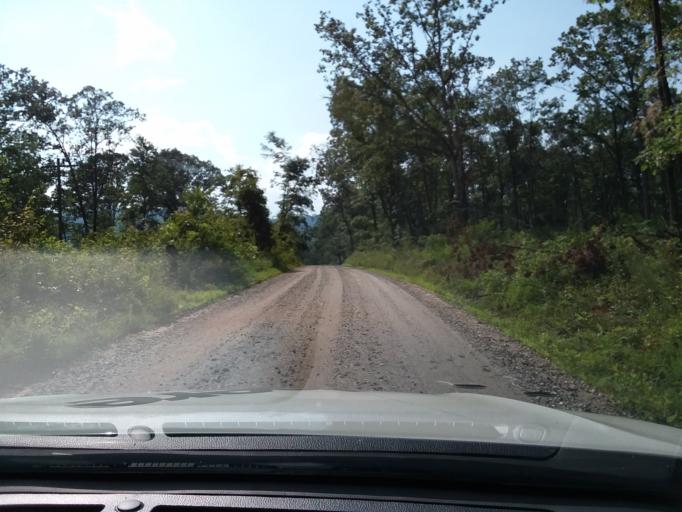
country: US
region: Georgia
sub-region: Habersham County
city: Clarkesville
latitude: 34.7182
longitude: -83.4392
